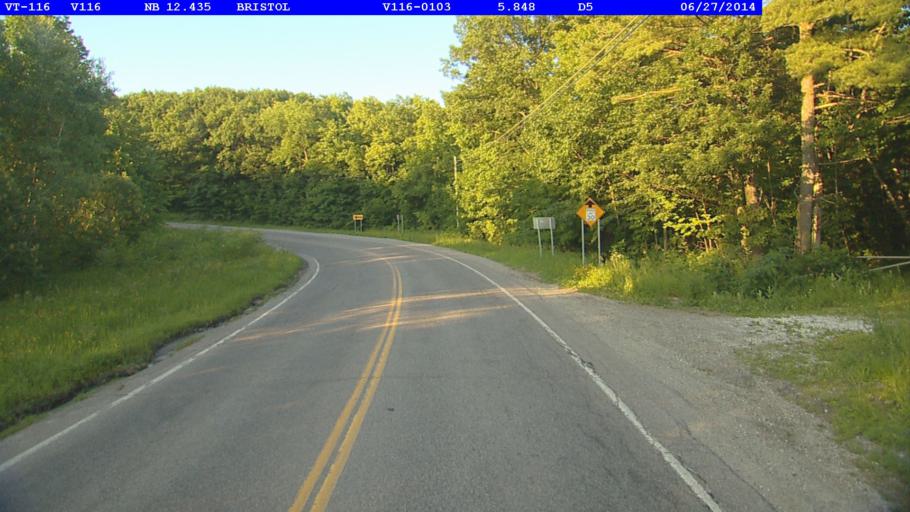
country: US
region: Vermont
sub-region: Addison County
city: Bristol
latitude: 44.1303
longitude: -73.0903
